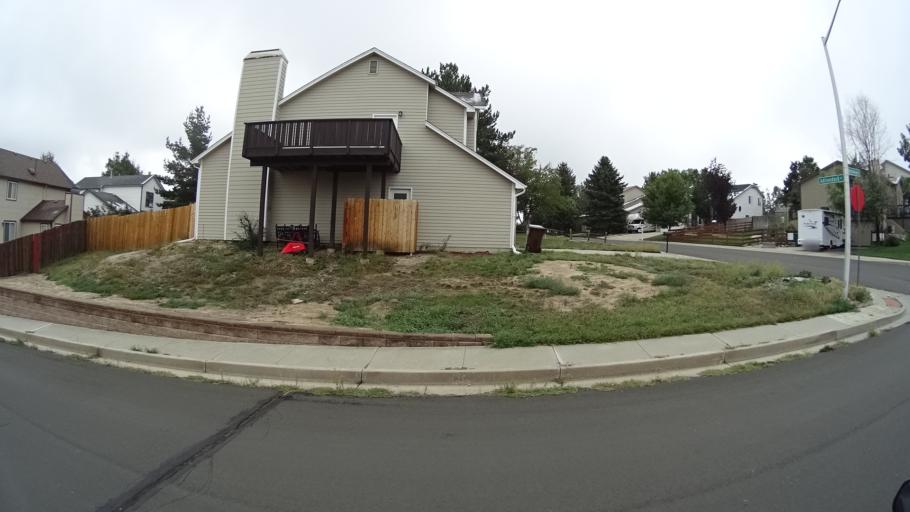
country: US
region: Colorado
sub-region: El Paso County
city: Cimarron Hills
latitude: 38.9220
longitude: -104.7581
